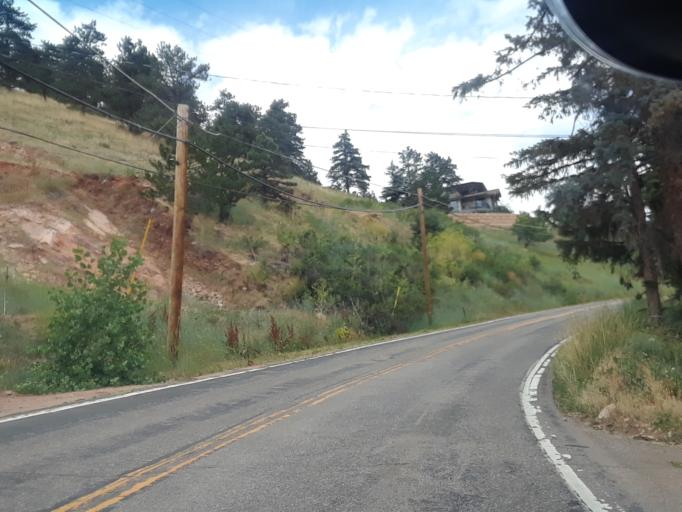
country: US
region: Colorado
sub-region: Boulder County
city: Boulder
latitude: 40.0841
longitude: -105.3025
